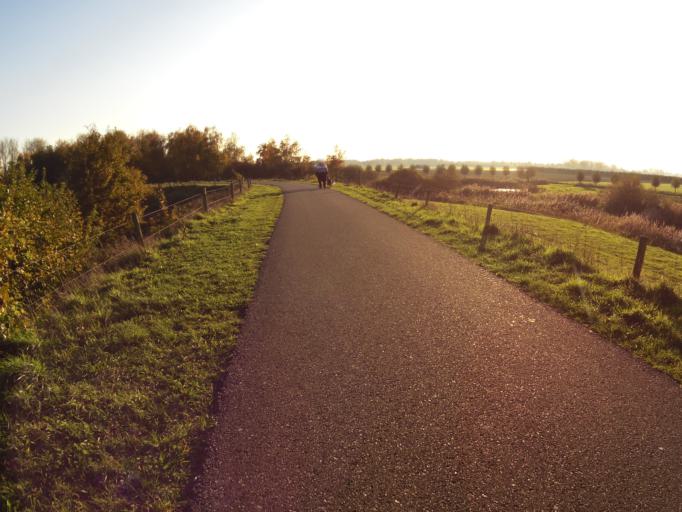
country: NL
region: North Brabant
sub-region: Gemeente Heusden
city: Heusden
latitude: 51.7037
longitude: 5.1125
